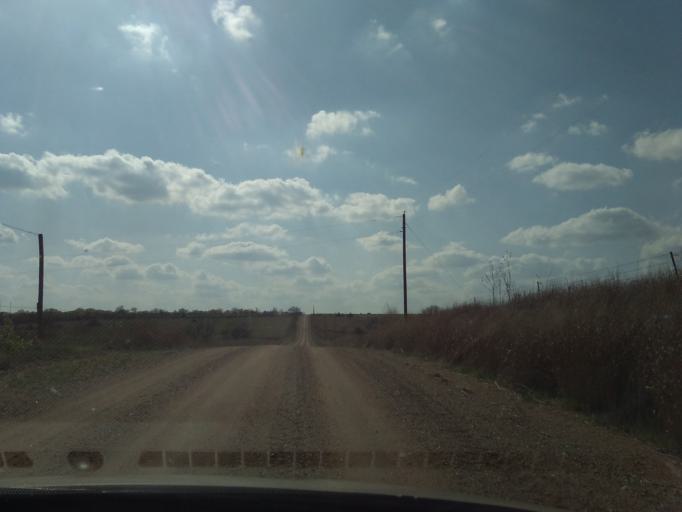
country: US
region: Nebraska
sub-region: Webster County
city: Red Cloud
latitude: 40.0314
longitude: -98.4370
